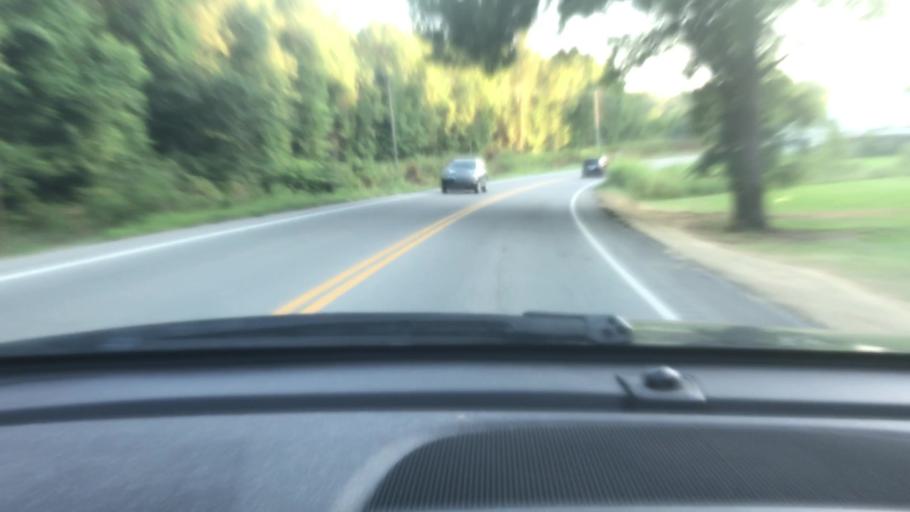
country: US
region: Tennessee
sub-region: Dickson County
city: Dickson
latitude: 36.1204
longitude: -87.3639
